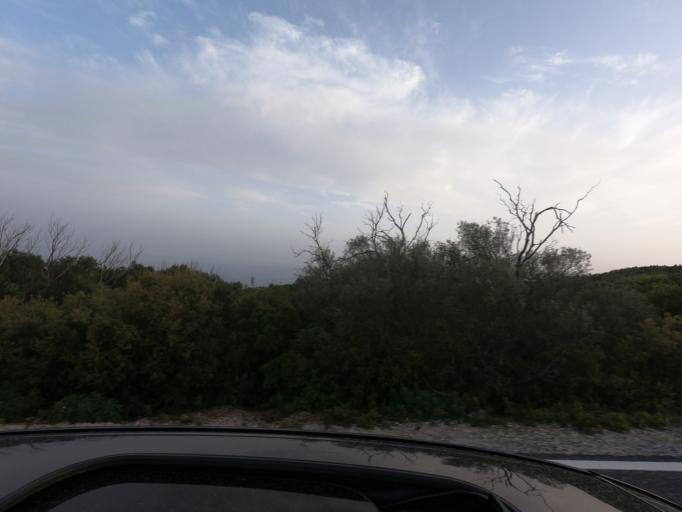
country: PT
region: Setubal
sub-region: Setubal
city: Setubal
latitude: 38.4891
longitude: -8.9496
